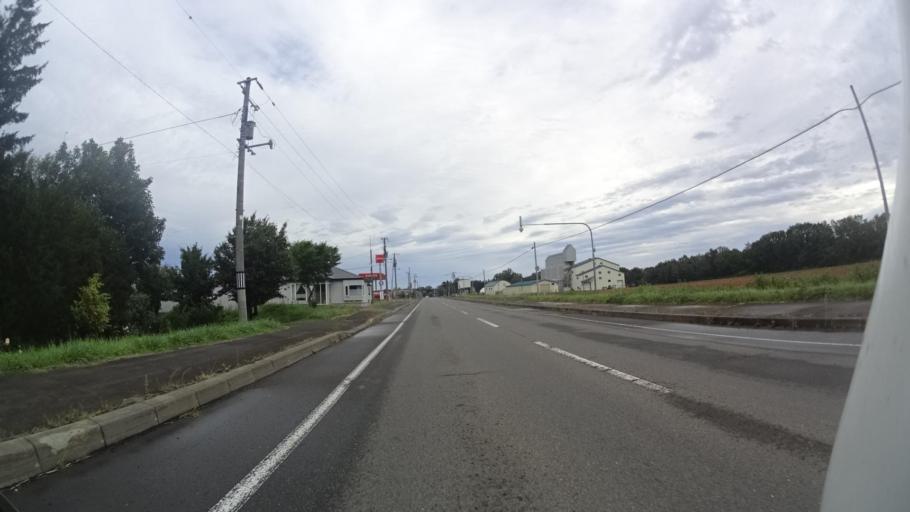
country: JP
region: Hokkaido
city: Abashiri
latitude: 43.8448
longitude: 144.5970
